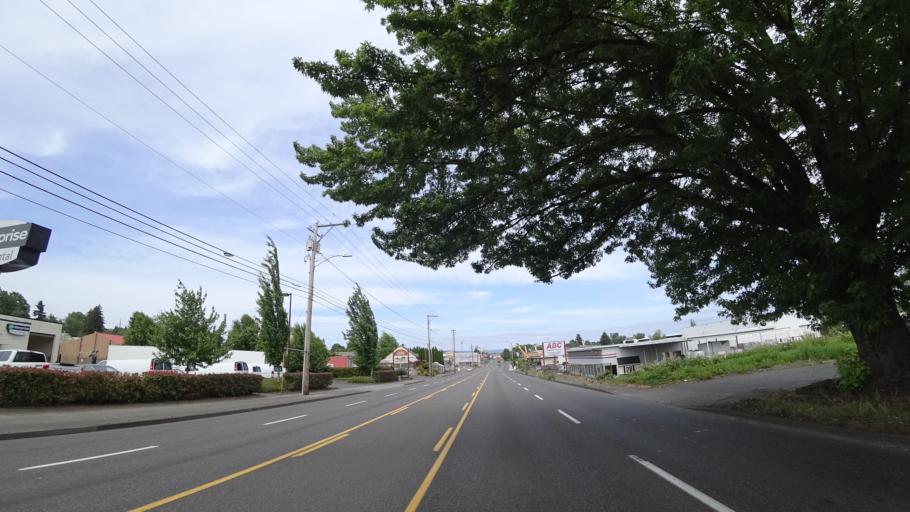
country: US
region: Oregon
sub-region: Multnomah County
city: Portland
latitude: 45.5768
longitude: -122.6450
